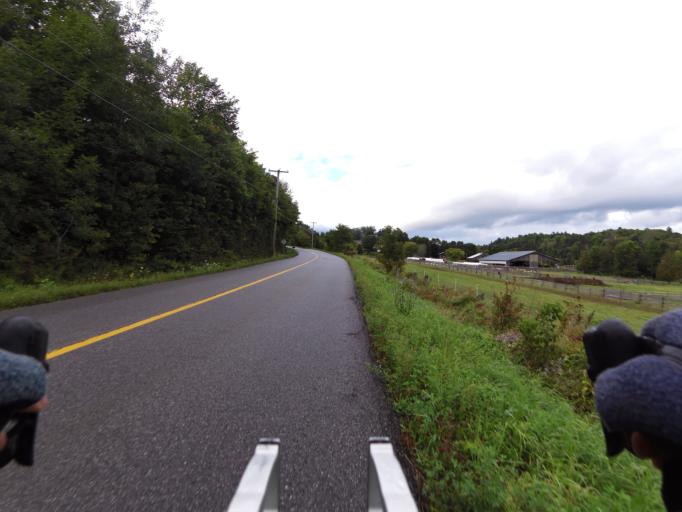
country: CA
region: Quebec
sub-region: Outaouais
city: Wakefield
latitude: 45.7298
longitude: -75.9715
